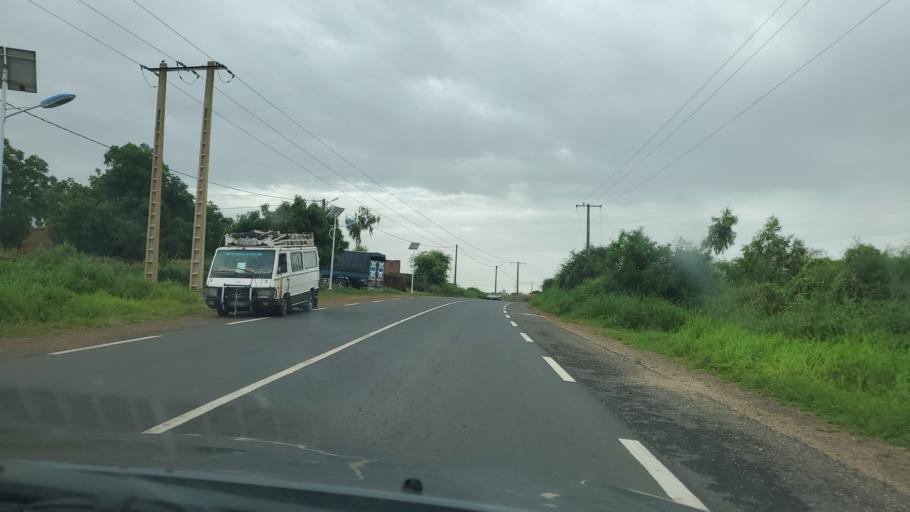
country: SN
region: Thies
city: Kayar
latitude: 15.1049
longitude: -16.9145
